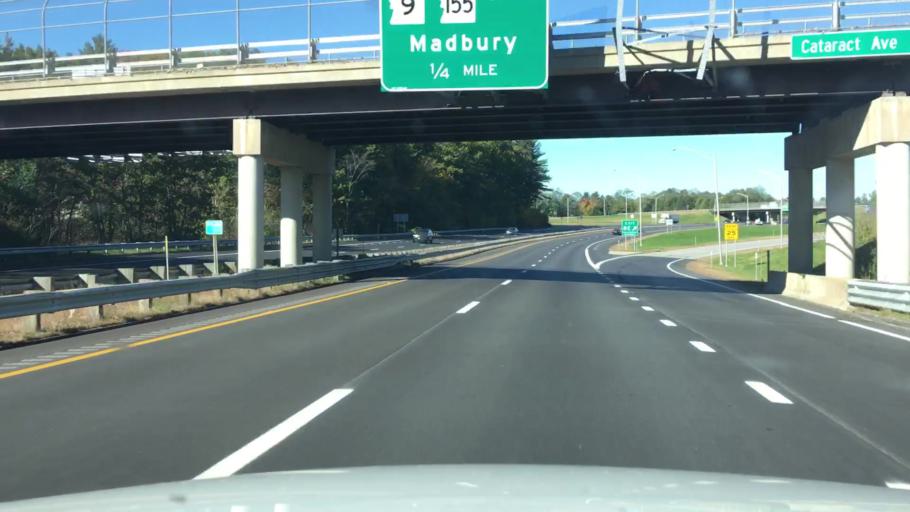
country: US
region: New Hampshire
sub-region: Strafford County
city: Dover
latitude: 43.1830
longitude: -70.8824
